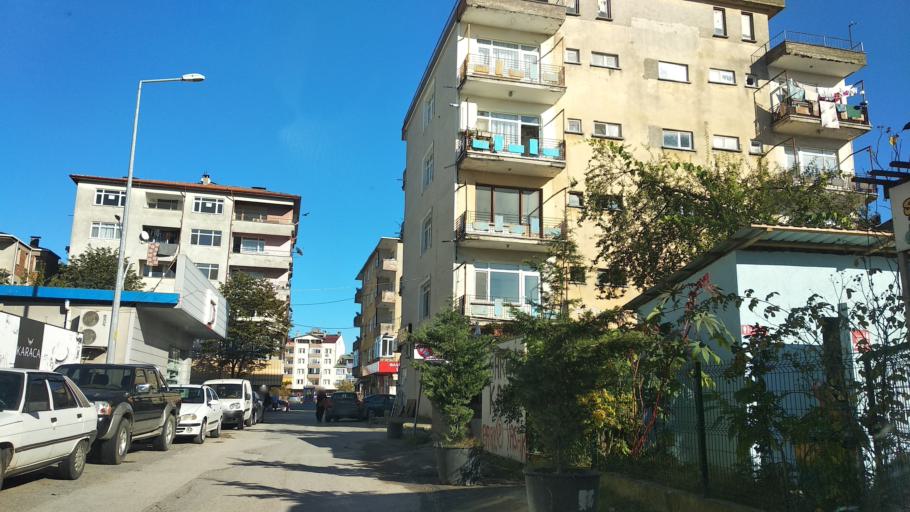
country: TR
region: Sakarya
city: Karasu
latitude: 41.0966
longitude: 30.6919
